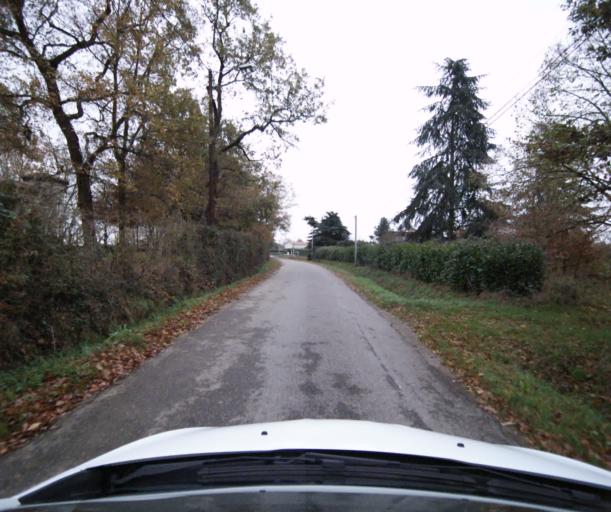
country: FR
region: Midi-Pyrenees
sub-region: Departement du Tarn-et-Garonne
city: Moissac
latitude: 44.0772
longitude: 1.1047
